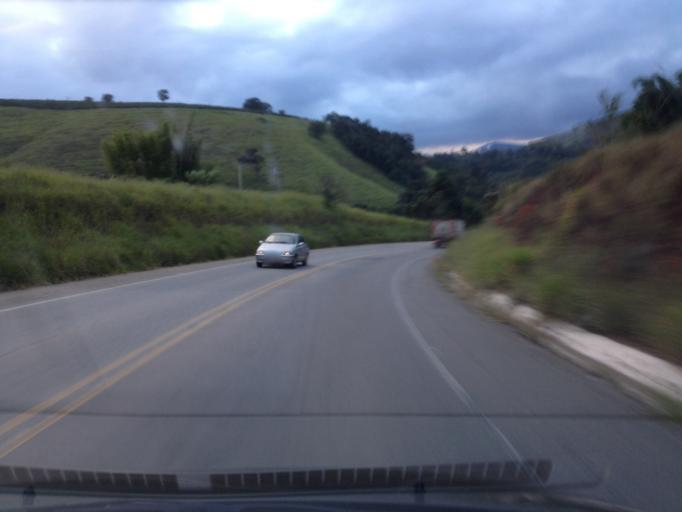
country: BR
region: Minas Gerais
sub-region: Sao Lourenco
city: Sao Lourenco
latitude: -22.0705
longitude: -45.0382
